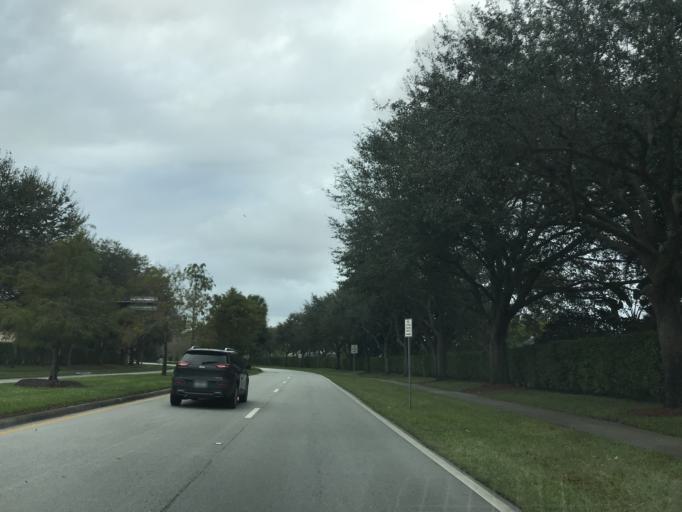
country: US
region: Florida
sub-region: Broward County
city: Parkland
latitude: 26.2987
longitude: -80.2400
